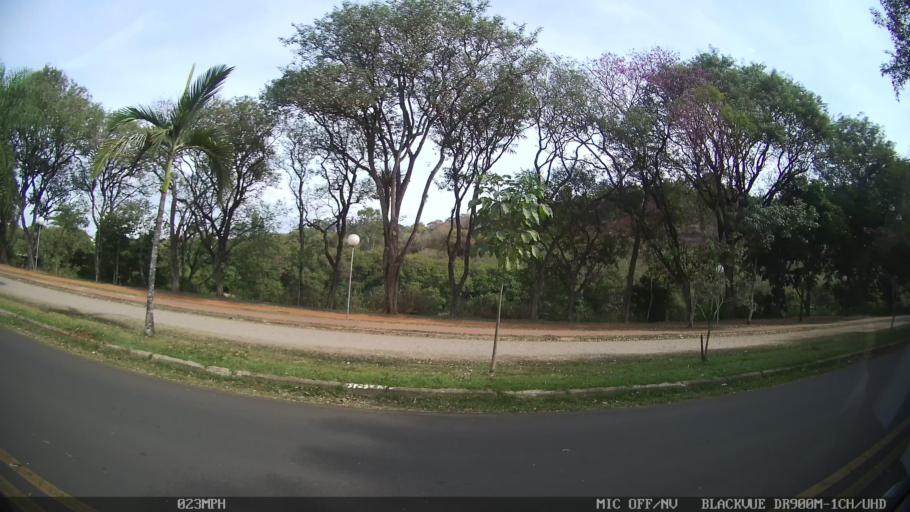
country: BR
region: Sao Paulo
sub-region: Piracicaba
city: Piracicaba
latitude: -22.7176
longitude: -47.6756
